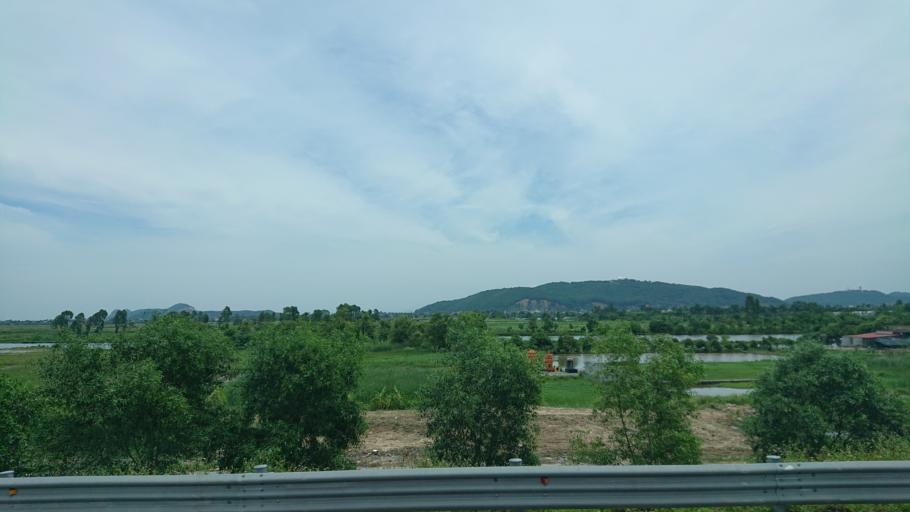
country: VN
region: Hai Phong
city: Nui Doi
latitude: 20.7708
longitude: 106.6074
